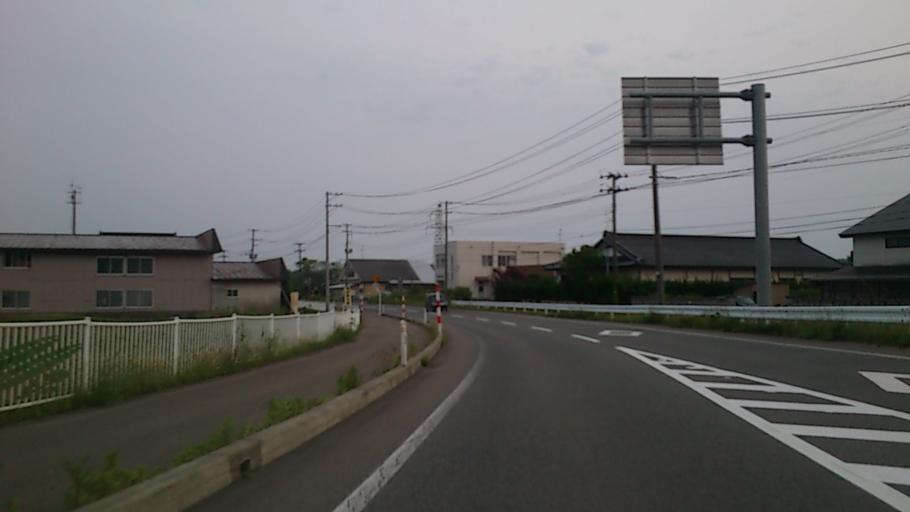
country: JP
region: Akita
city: Noshiromachi
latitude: 40.1010
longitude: 140.0792
